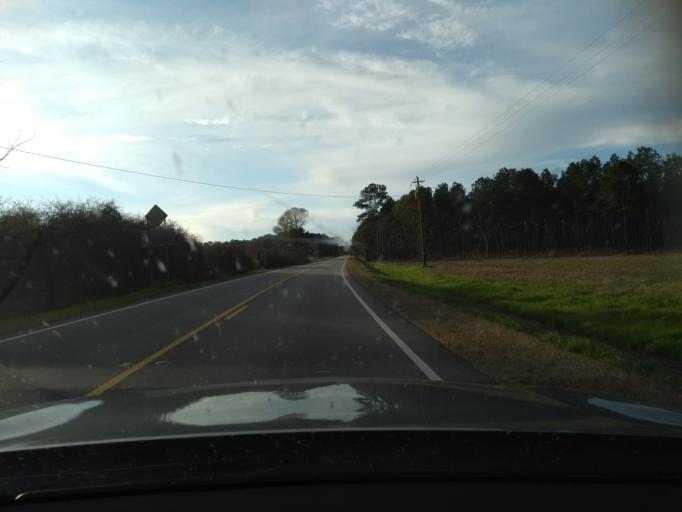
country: US
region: Georgia
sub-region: Bulloch County
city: Brooklet
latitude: 32.2886
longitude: -81.7585
